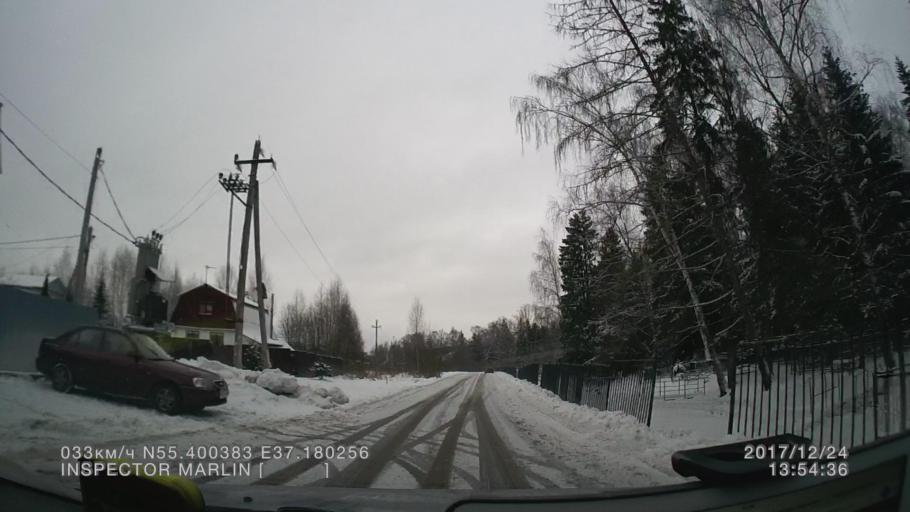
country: RU
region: Moskovskaya
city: Troitsk
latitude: 55.4004
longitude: 37.1800
